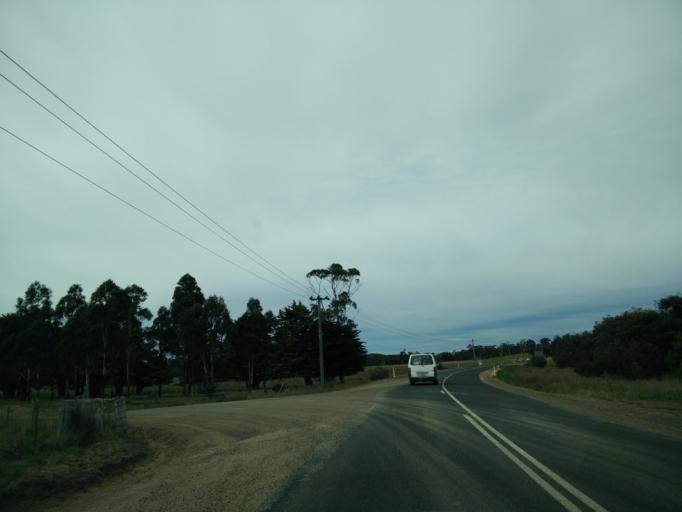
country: AU
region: Tasmania
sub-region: Break O'Day
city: St Helens
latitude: -41.9089
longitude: 148.2526
